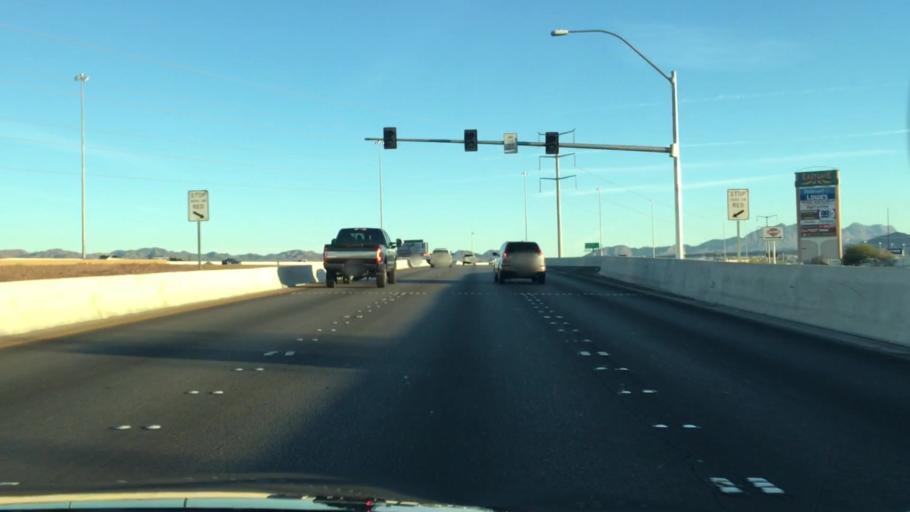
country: US
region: Nevada
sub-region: Clark County
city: Whitney
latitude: 36.0622
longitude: -115.0324
